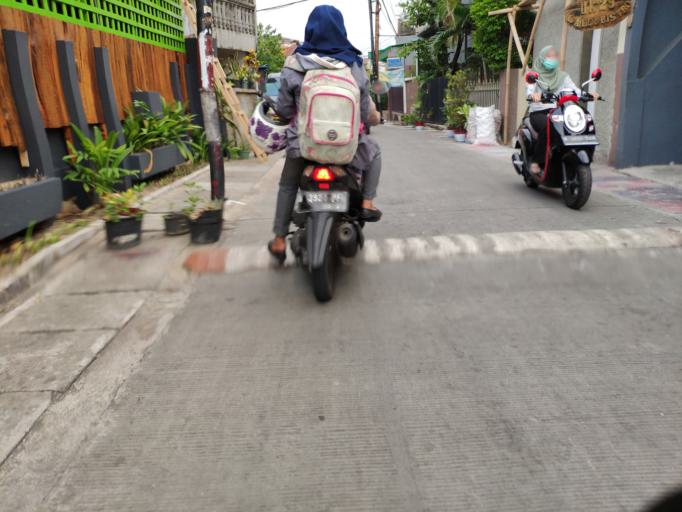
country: ID
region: Jakarta Raya
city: Jakarta
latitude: -6.1984
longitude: 106.8665
